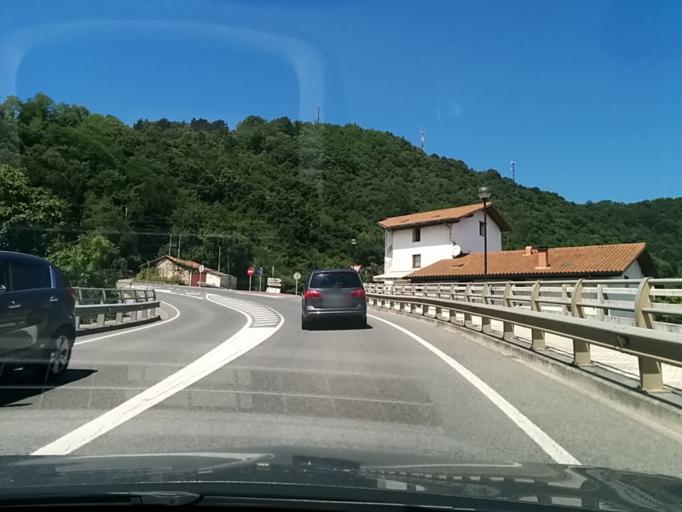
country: ES
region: Basque Country
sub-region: Provincia de Guipuzcoa
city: Orio
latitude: 43.2746
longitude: -2.1307
